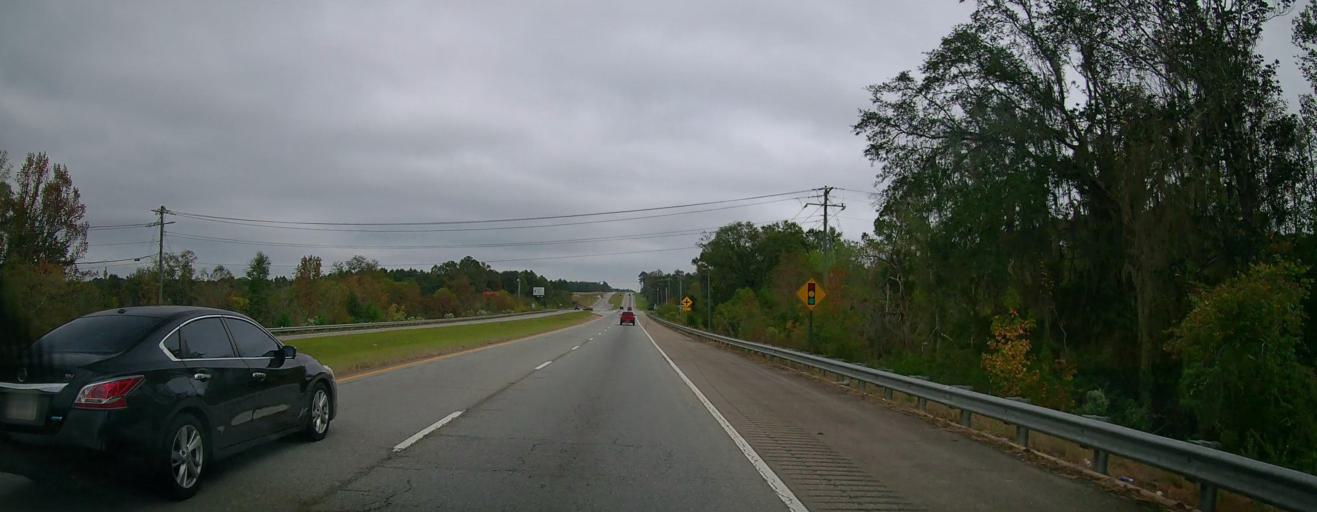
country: US
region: Georgia
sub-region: Thomas County
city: Thomasville
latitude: 30.8749
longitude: -83.9806
